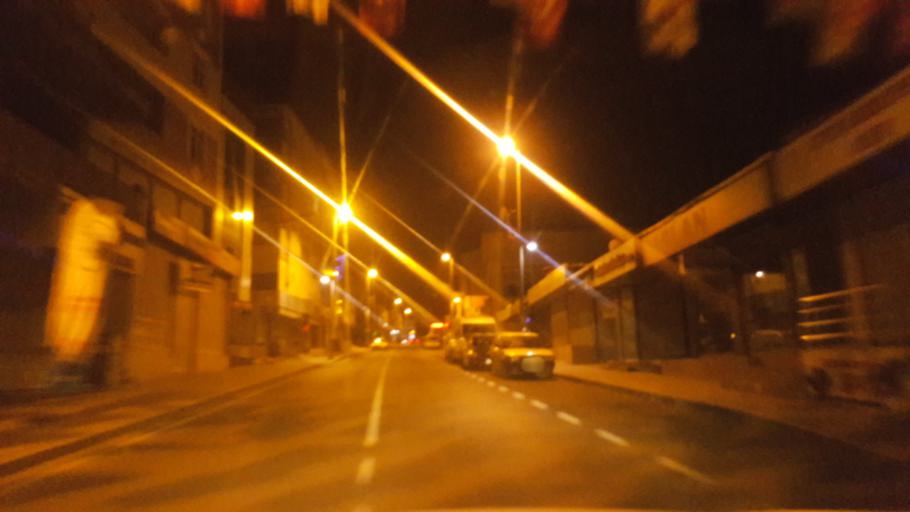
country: TR
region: Kocaeli
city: Tavsancil
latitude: 40.7861
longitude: 29.5382
